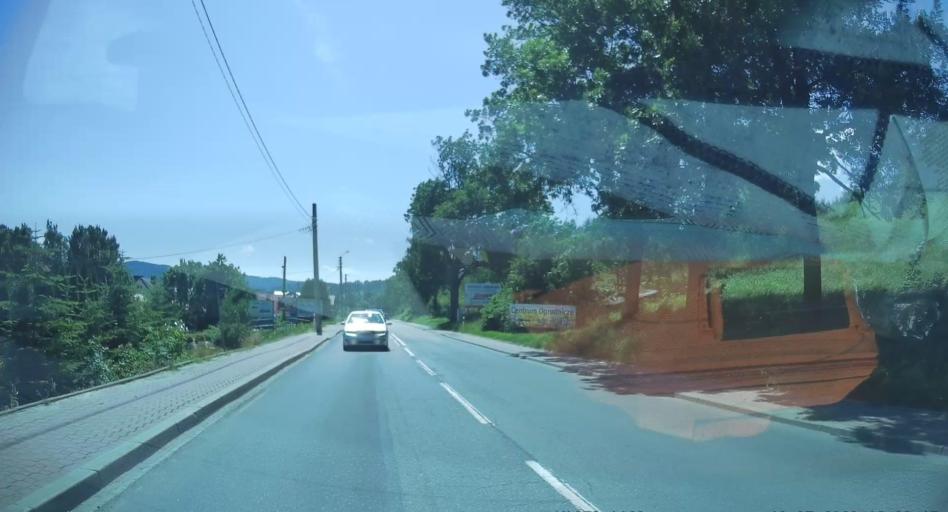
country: PL
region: Lesser Poland Voivodeship
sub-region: Powiat nowosadecki
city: Krynica-Zdroj
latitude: 49.3927
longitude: 20.9547
